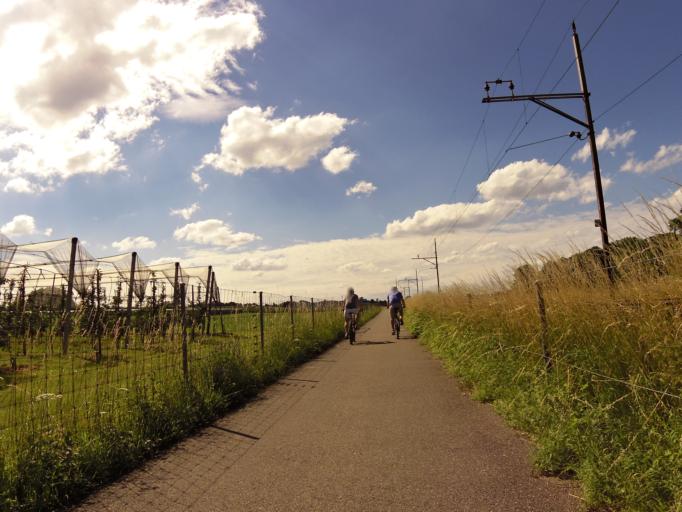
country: CH
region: Thurgau
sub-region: Arbon District
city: Egnach
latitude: 47.5401
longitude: 9.3924
